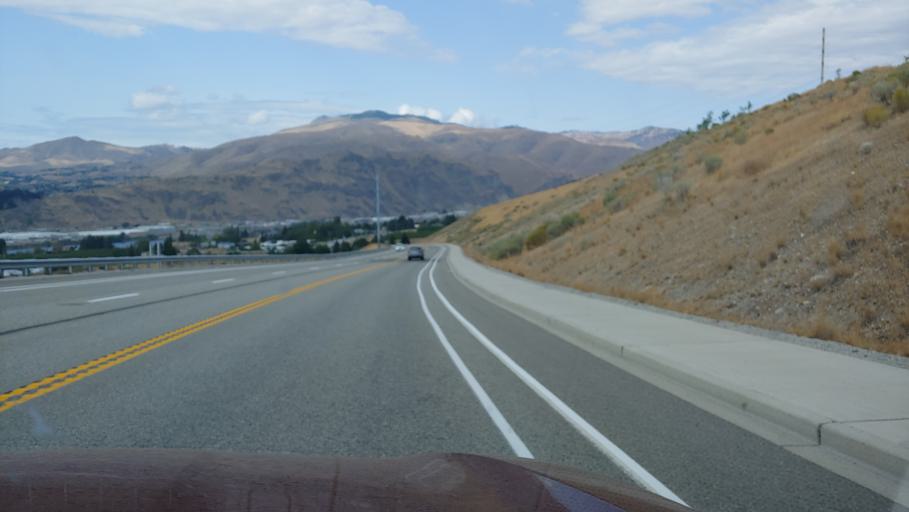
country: US
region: Washington
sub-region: Douglas County
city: East Wenatchee Bench
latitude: 47.4615
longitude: -120.2930
